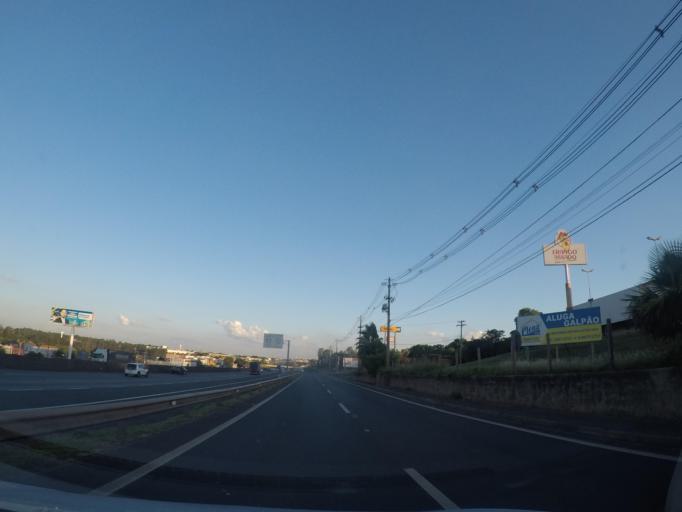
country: BR
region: Sao Paulo
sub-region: Hortolandia
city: Hortolandia
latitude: -22.8147
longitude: -47.2082
